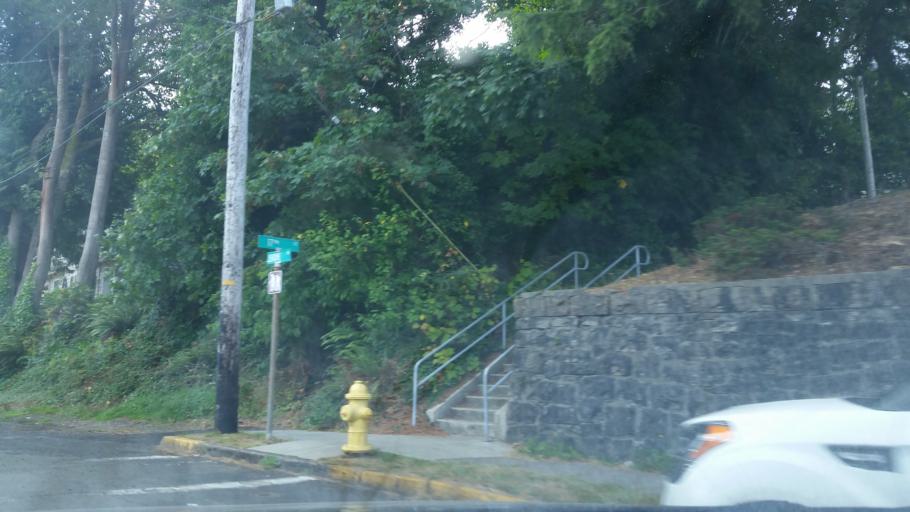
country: US
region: Oregon
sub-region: Clatsop County
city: Astoria
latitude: 46.1842
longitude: -123.8241
